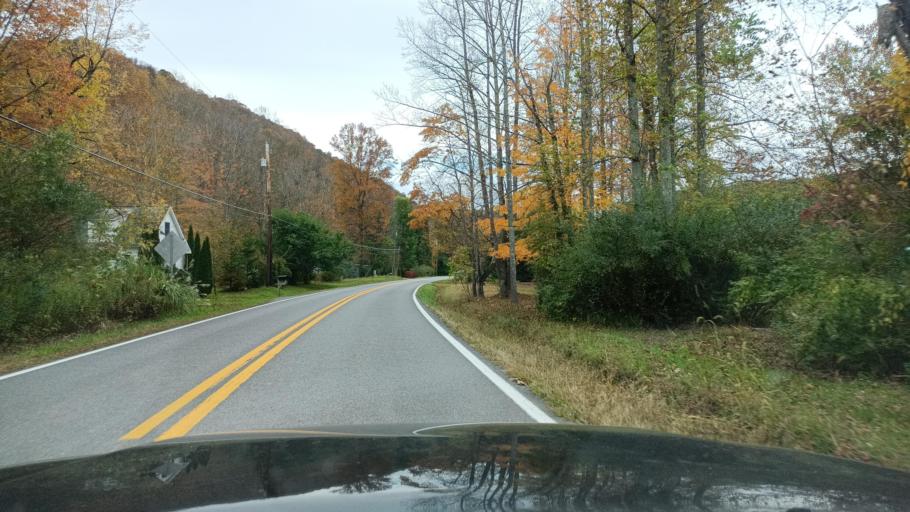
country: US
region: West Virginia
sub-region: Preston County
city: Kingwood
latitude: 39.3144
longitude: -79.6513
